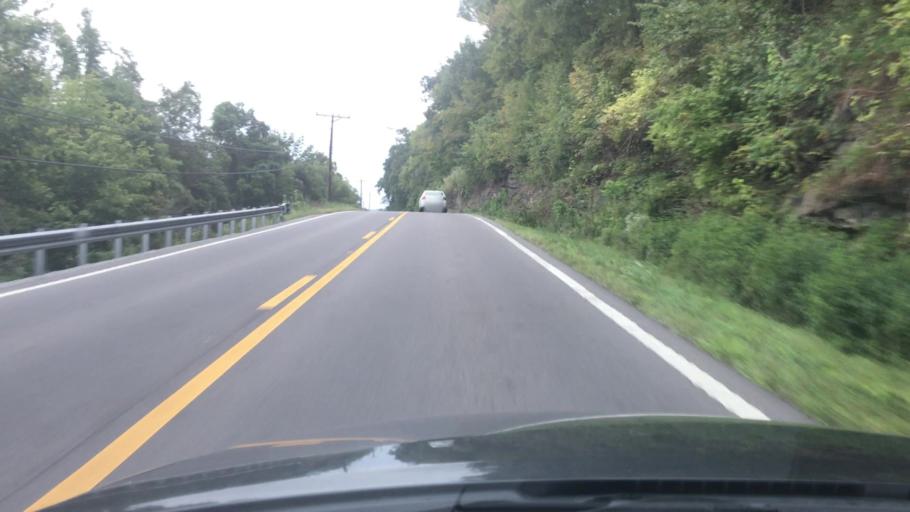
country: US
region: Tennessee
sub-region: Cheatham County
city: Ashland City
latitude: 36.2743
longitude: -87.0883
